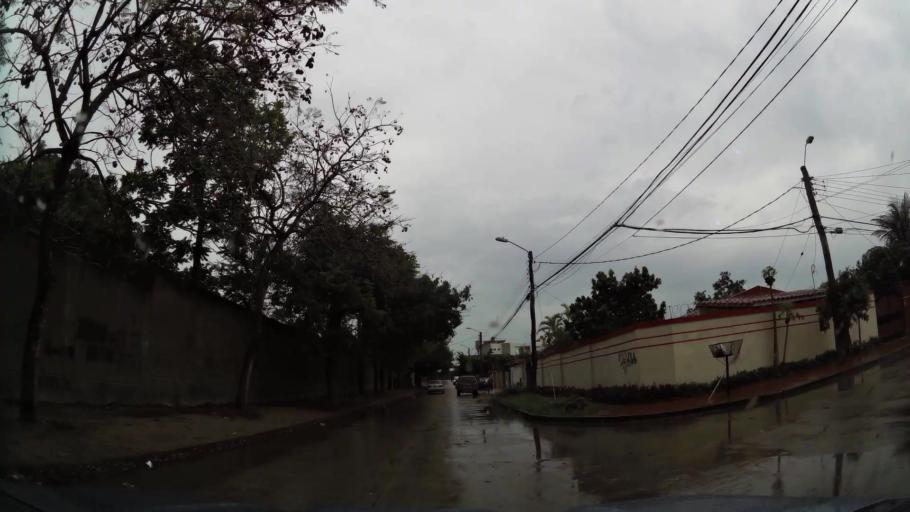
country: BO
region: Santa Cruz
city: Santa Cruz de la Sierra
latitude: -17.8103
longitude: -63.2272
